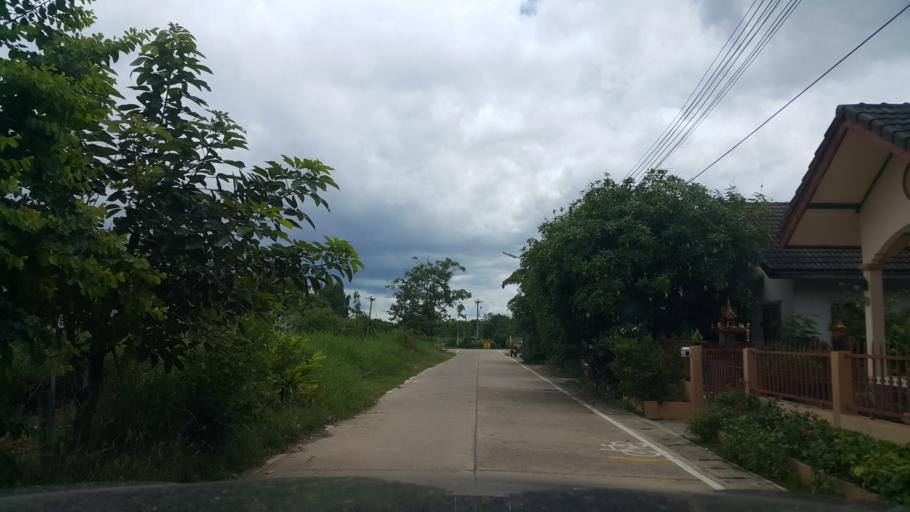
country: TH
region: Sukhothai
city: Sukhothai
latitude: 17.0162
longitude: 99.8090
